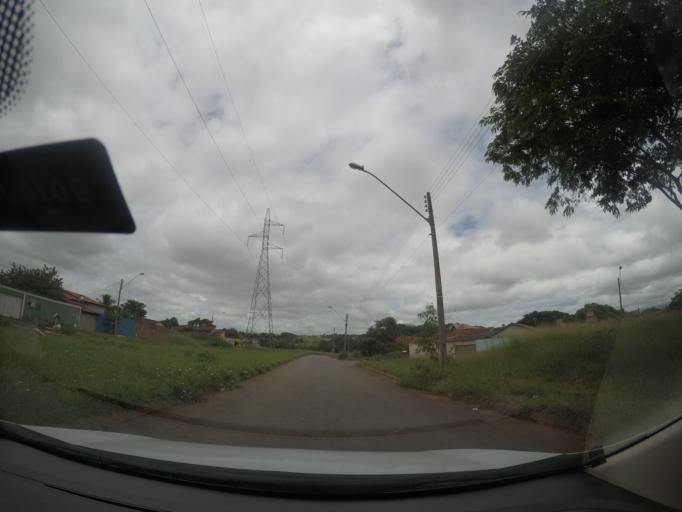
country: BR
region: Goias
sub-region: Goiania
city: Goiania
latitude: -16.7396
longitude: -49.3718
